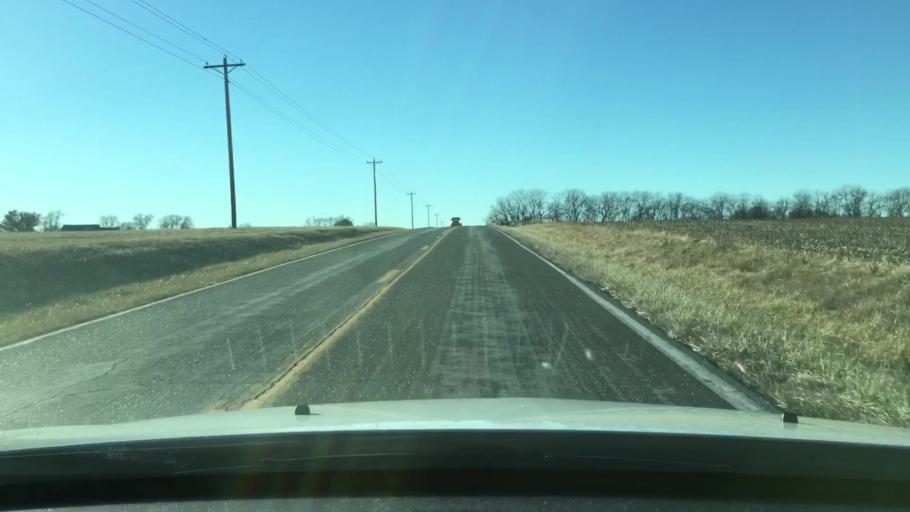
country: US
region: Missouri
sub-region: Audrain County
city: Mexico
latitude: 39.2765
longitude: -91.7869
